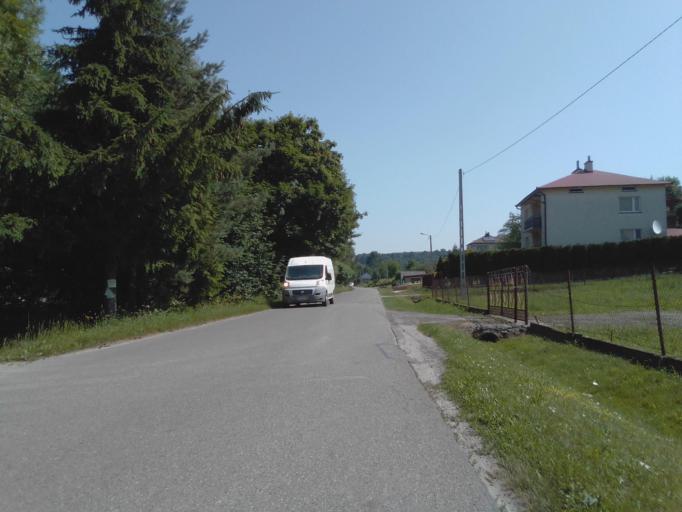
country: PL
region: Subcarpathian Voivodeship
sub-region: Powiat ropczycko-sedziszowski
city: Zagorzyce
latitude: 50.0335
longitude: 21.6511
